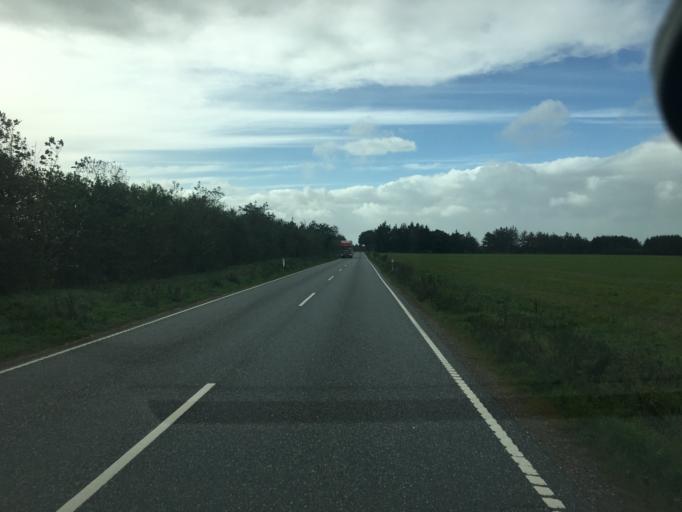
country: DK
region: South Denmark
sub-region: Tonder Kommune
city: Tonder
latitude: 55.0125
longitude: 8.8408
